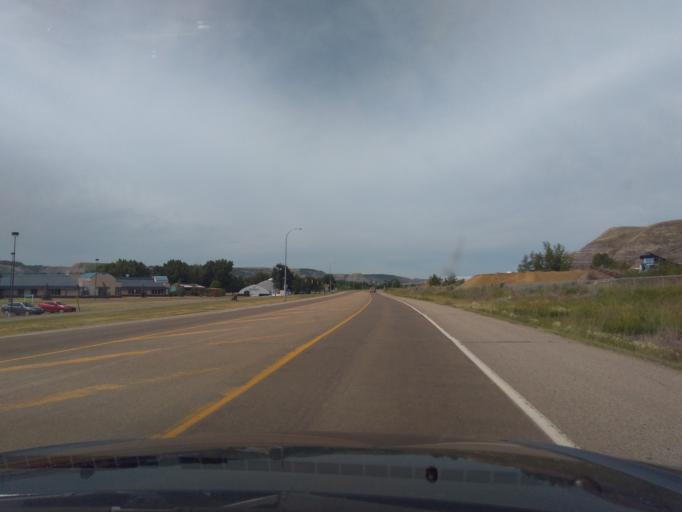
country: CA
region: Alberta
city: Three Hills
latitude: 51.4714
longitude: -112.7242
